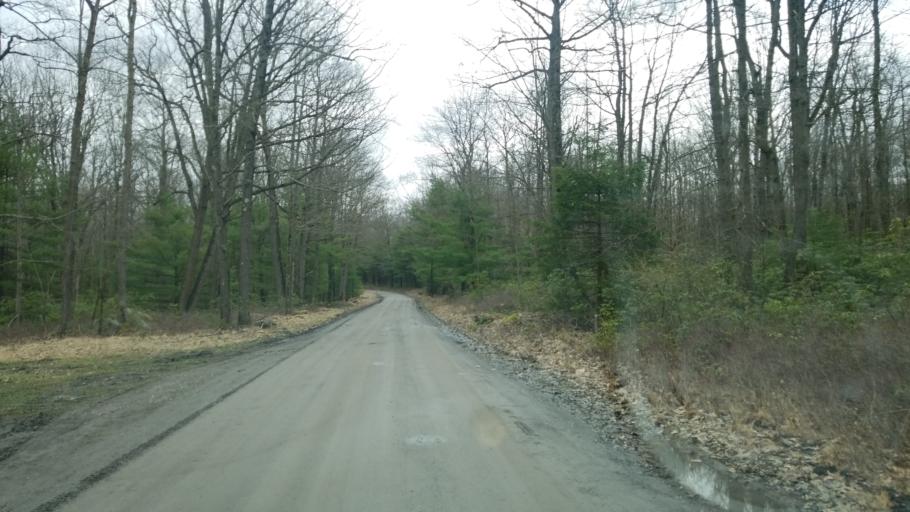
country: US
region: Pennsylvania
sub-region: Clearfield County
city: Shiloh
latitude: 41.1662
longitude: -78.2542
